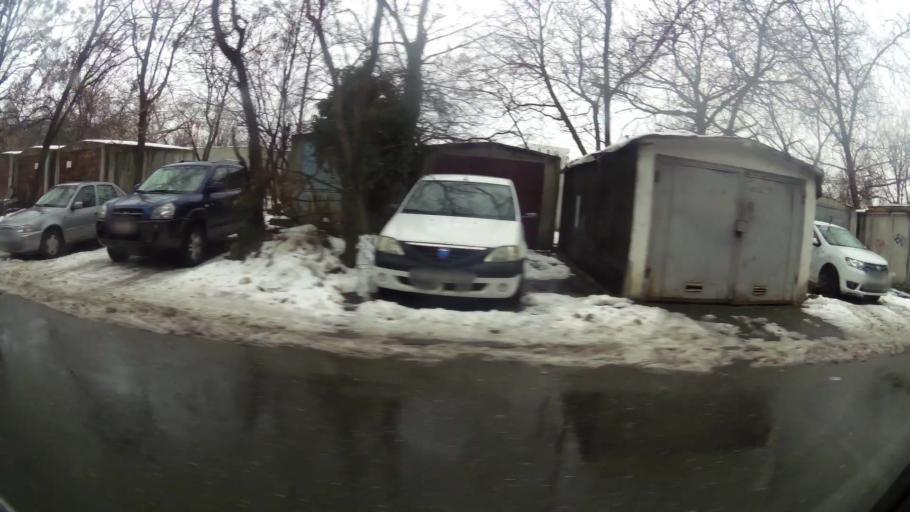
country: RO
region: Ilfov
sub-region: Comuna Chiajna
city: Rosu
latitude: 44.4376
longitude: 26.0419
